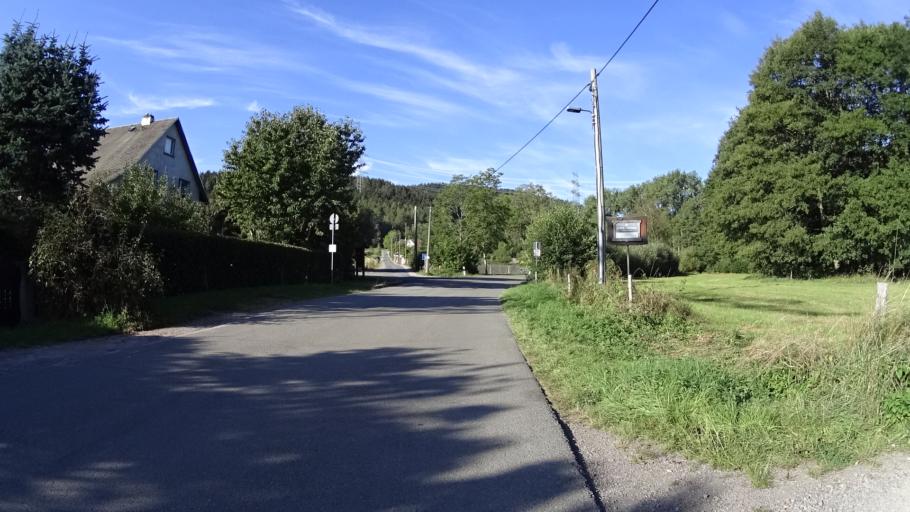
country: DE
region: Thuringia
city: Mohrenbach
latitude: 50.6443
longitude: 10.9908
